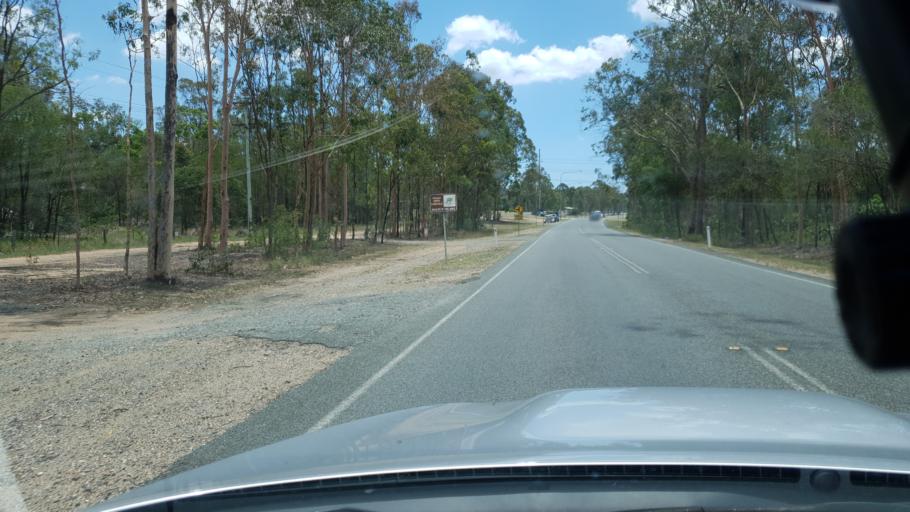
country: AU
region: Queensland
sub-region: Logan
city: North Maclean
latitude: -27.7326
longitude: 152.9847
